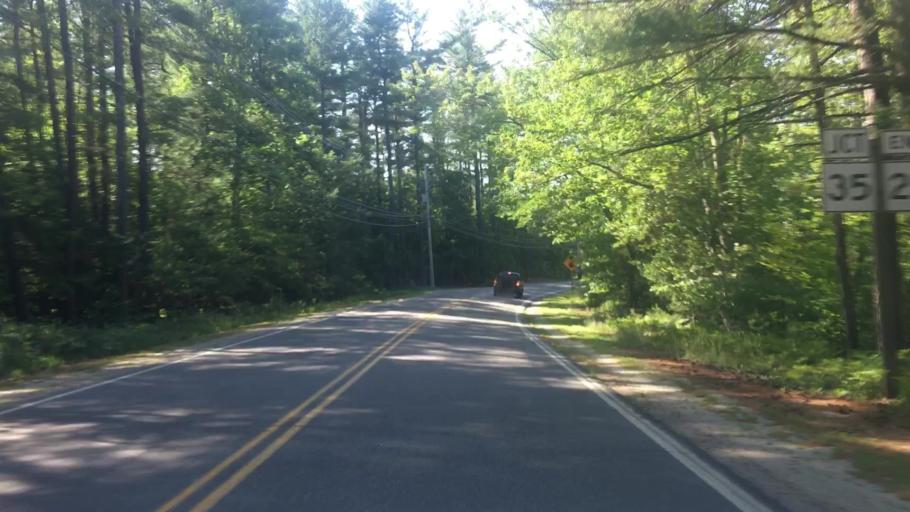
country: US
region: Maine
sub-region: York County
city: Hollis Center
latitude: 43.6906
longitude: -70.5955
